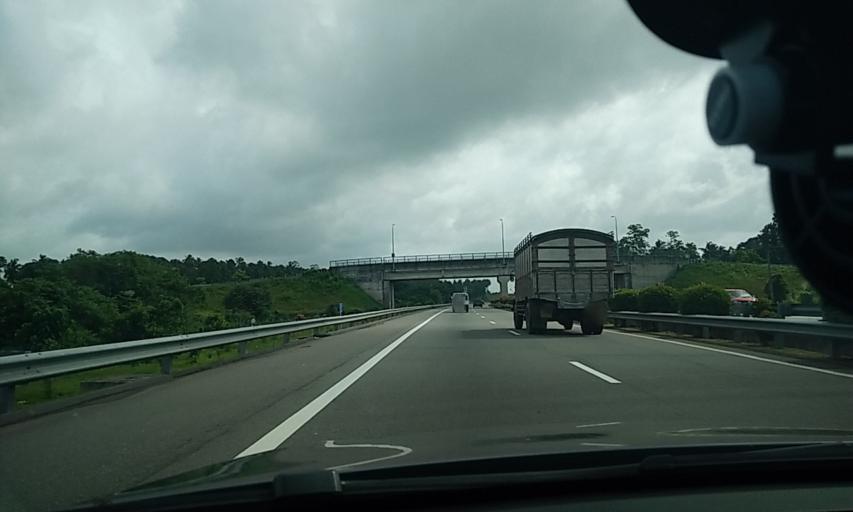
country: LK
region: Western
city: Homagama
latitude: 6.8570
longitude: 79.9777
